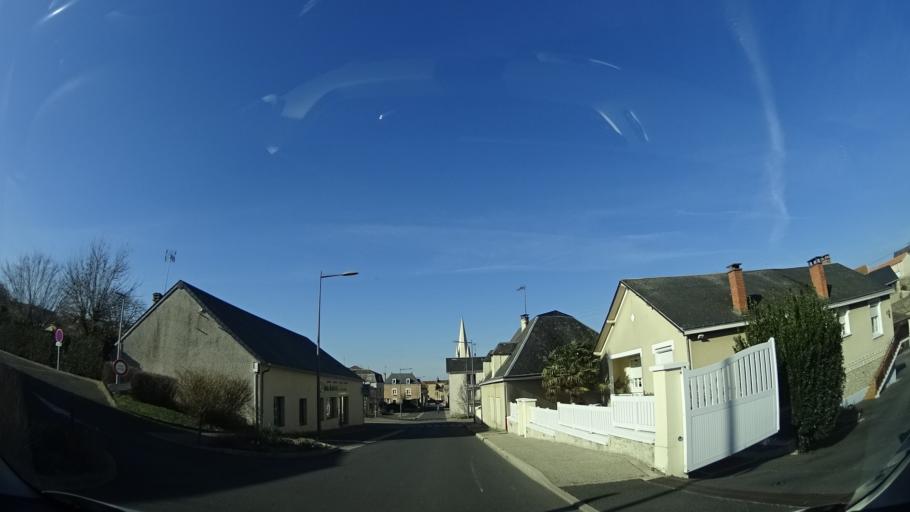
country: FR
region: Poitou-Charentes
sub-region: Departement des Deux-Sevres
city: Airvault
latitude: 46.8270
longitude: -0.1341
